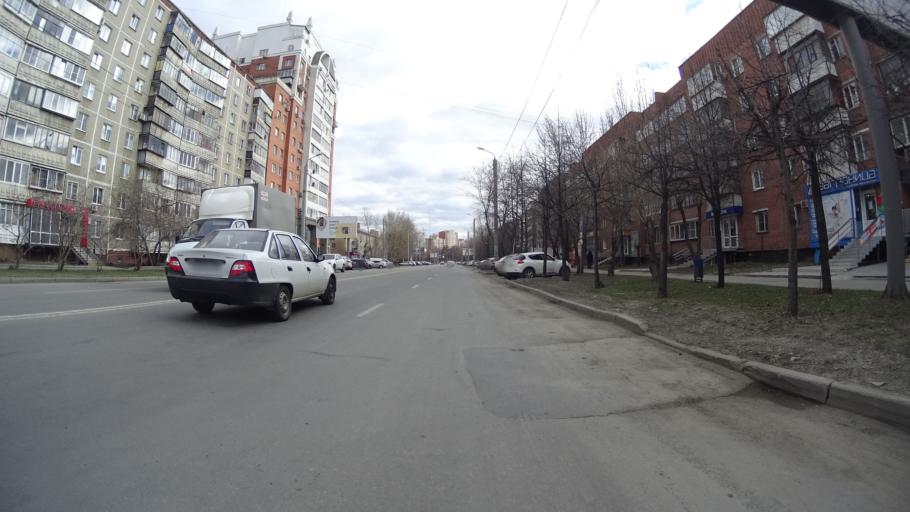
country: RU
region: Chelyabinsk
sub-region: Gorod Chelyabinsk
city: Chelyabinsk
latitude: 55.1517
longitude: 61.3804
